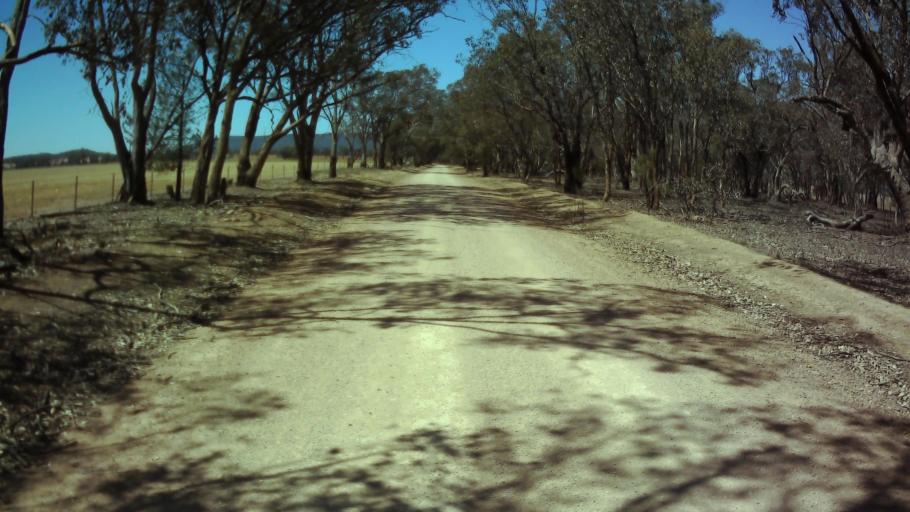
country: AU
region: New South Wales
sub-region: Weddin
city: Grenfell
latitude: -33.9196
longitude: 148.0789
